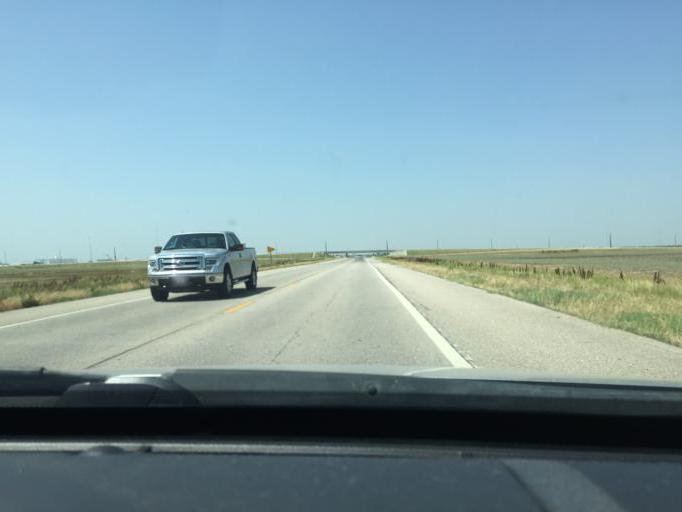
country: US
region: Kansas
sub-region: Reno County
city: Hutchinson
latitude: 38.0226
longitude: -97.8668
